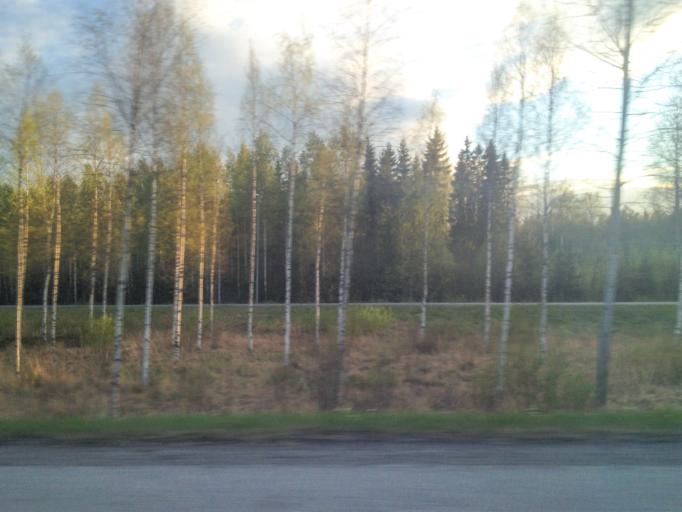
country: FI
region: Haeme
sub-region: Riihimaeki
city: Riihimaeki
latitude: 60.7535
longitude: 24.7293
